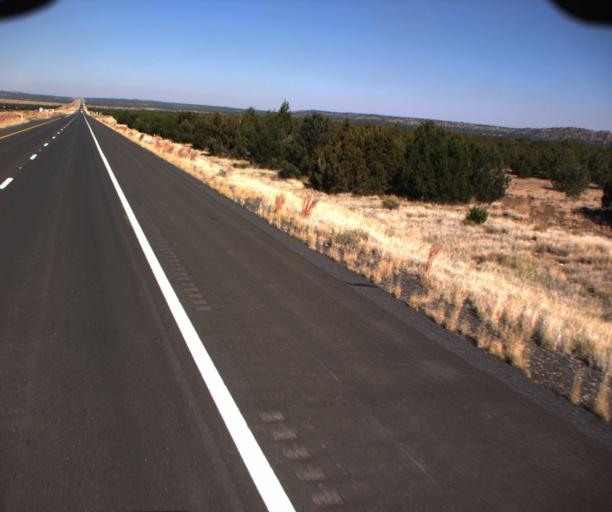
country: US
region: Arizona
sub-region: Coconino County
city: Flagstaff
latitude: 35.4239
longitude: -111.5698
